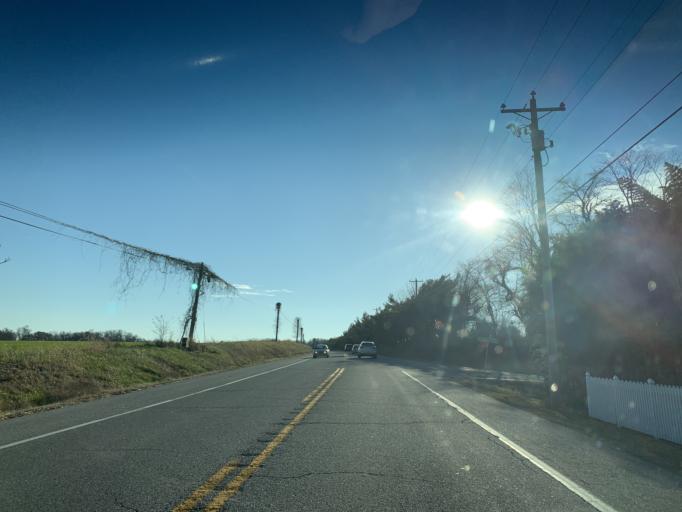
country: US
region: Delaware
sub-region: New Castle County
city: Middletown
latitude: 39.3787
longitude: -75.8798
